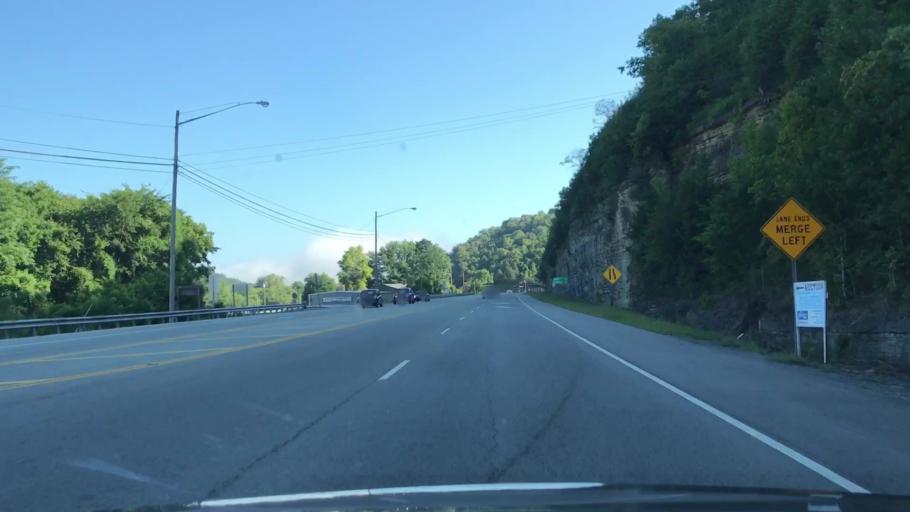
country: US
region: Tennessee
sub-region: Jackson County
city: Gainesboro
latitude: 36.3562
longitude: -85.6552
